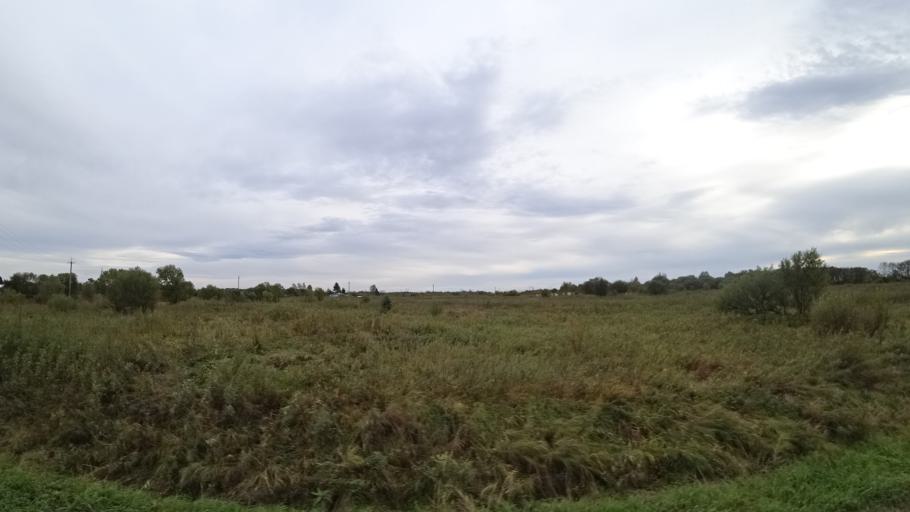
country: RU
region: Amur
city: Arkhara
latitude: 49.4366
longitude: 130.2610
